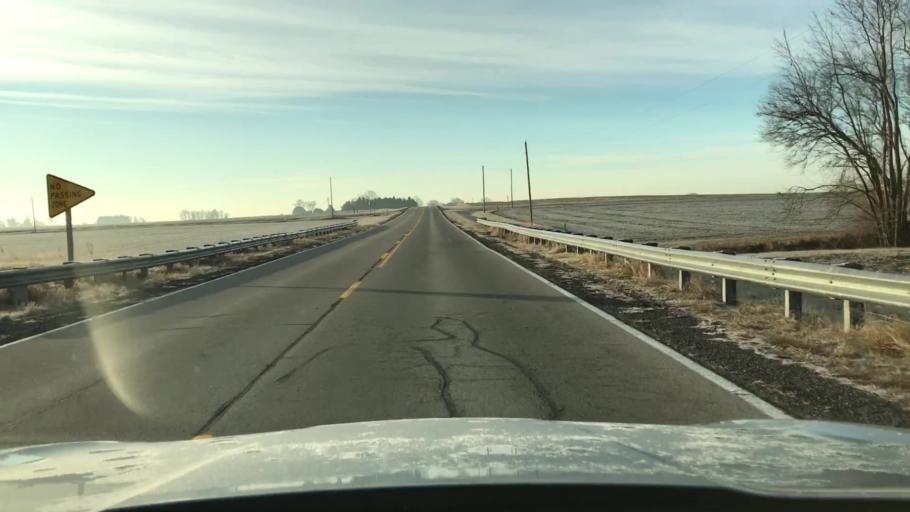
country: US
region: Illinois
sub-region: McLean County
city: Hudson
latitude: 40.6219
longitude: -88.9456
